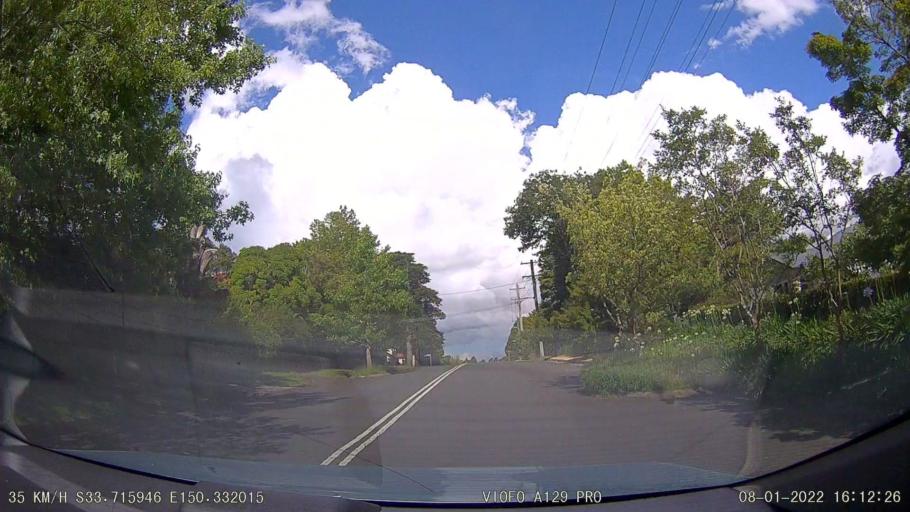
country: AU
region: New South Wales
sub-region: Blue Mountains Municipality
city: Leura
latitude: -33.7159
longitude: 150.3319
